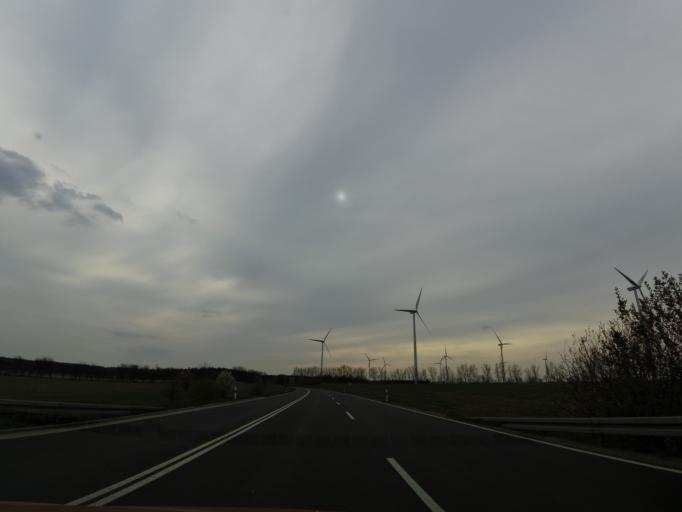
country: DE
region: Brandenburg
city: Beeskow
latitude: 52.1975
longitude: 14.2314
